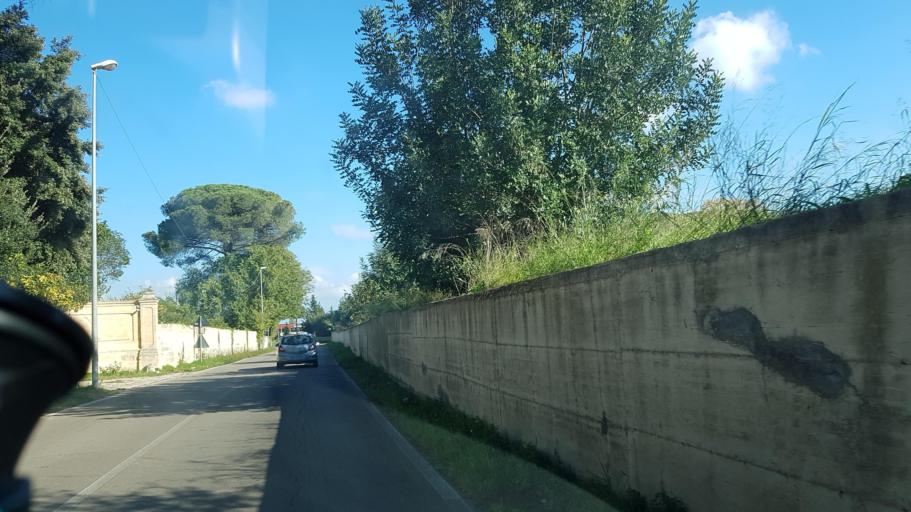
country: IT
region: Apulia
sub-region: Provincia di Lecce
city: Arnesano
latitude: 40.3328
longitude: 18.1011
